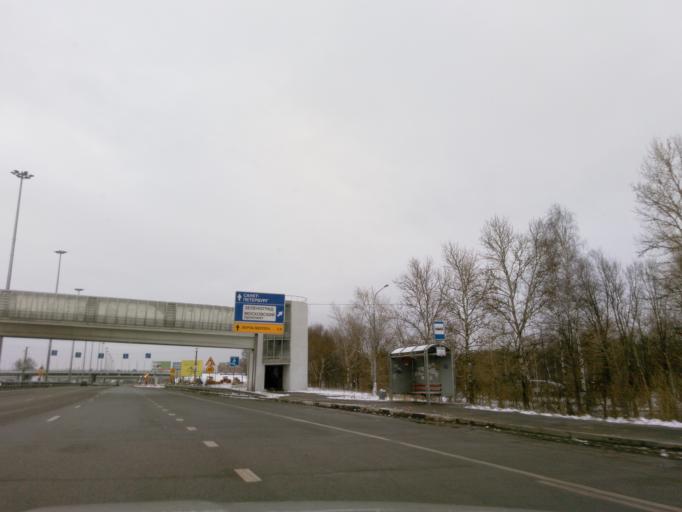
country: RU
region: Moskovskaya
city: Rzhavki
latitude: 56.0021
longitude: 37.2380
